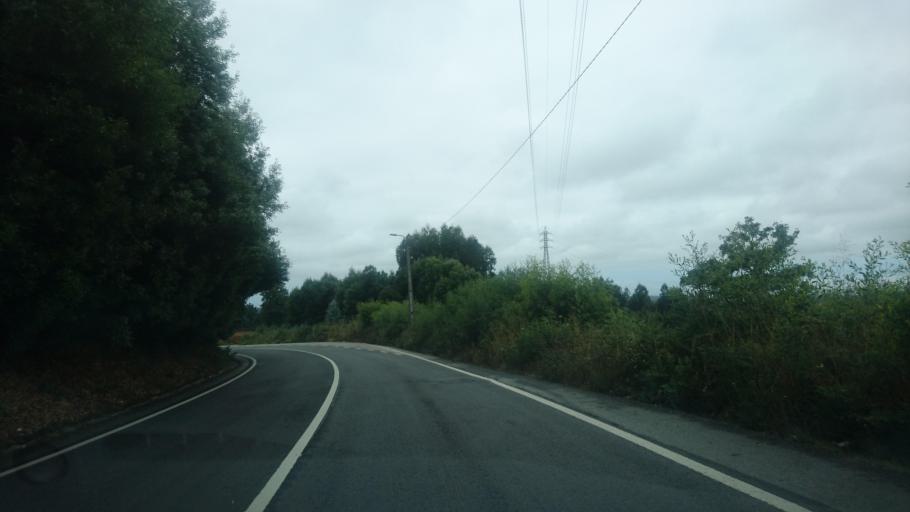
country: PT
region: Aveiro
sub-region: Santa Maria da Feira
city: Sao Joao de Ver
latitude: 40.9588
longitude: -8.5475
